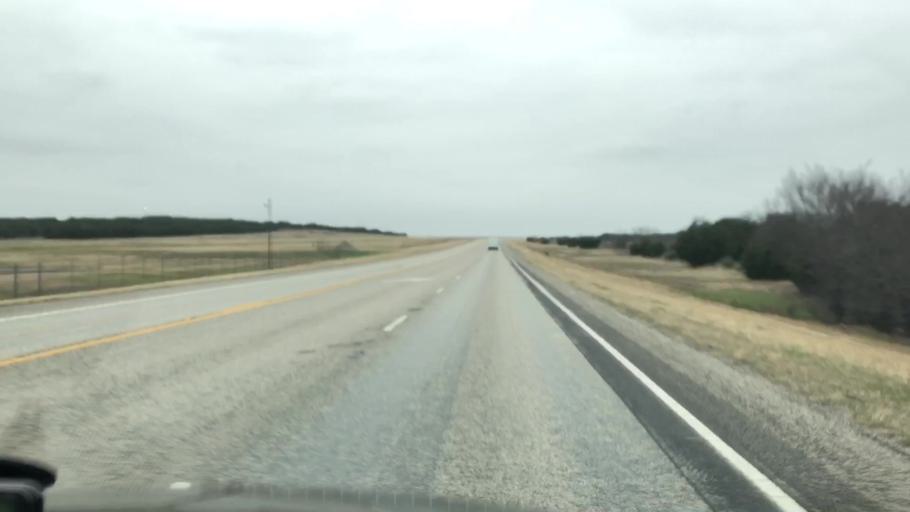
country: US
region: Texas
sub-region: Lampasas County
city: Lampasas
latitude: 31.1047
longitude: -98.1940
